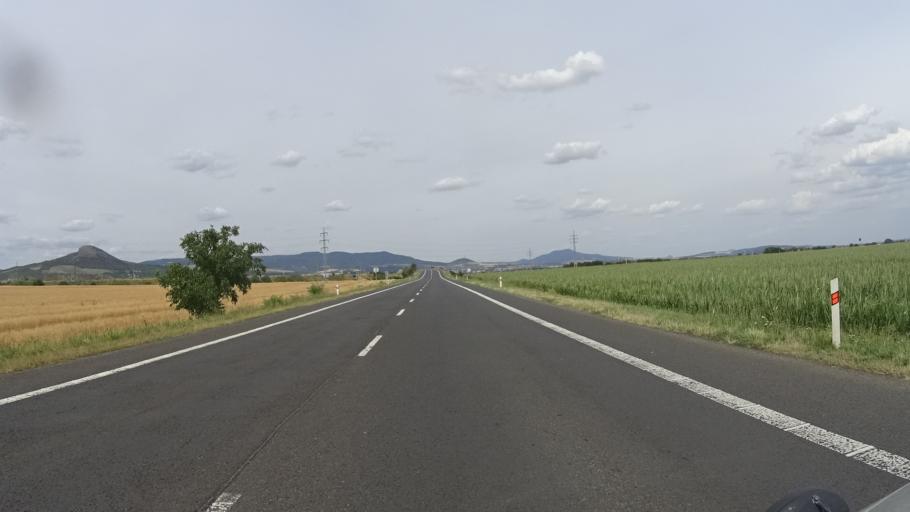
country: CZ
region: Ustecky
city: Lovosice
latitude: 50.4987
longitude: 14.0930
